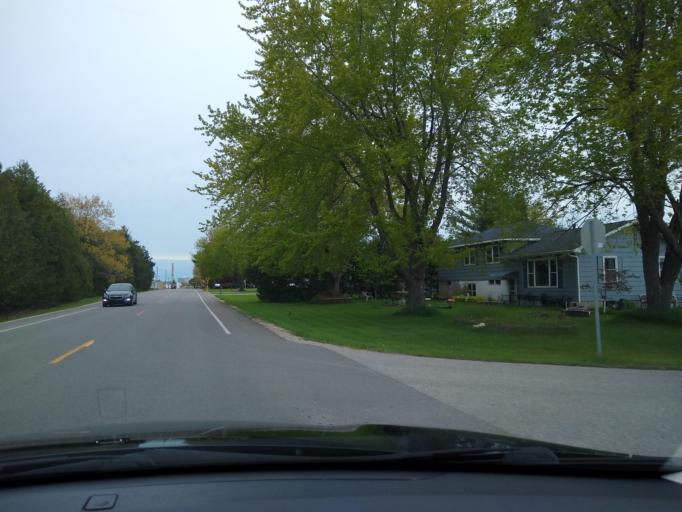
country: US
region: Michigan
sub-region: Delta County
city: Escanaba
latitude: 45.7863
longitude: -87.0783
